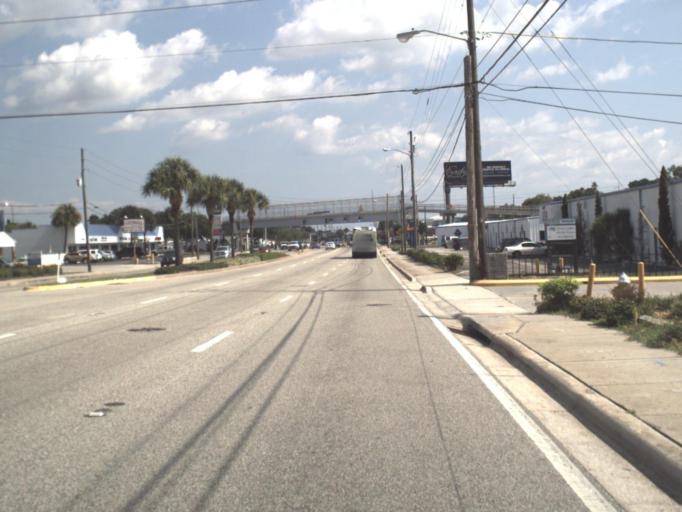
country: US
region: Florida
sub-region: Pinellas County
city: Seminole
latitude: 27.8302
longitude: -82.7869
